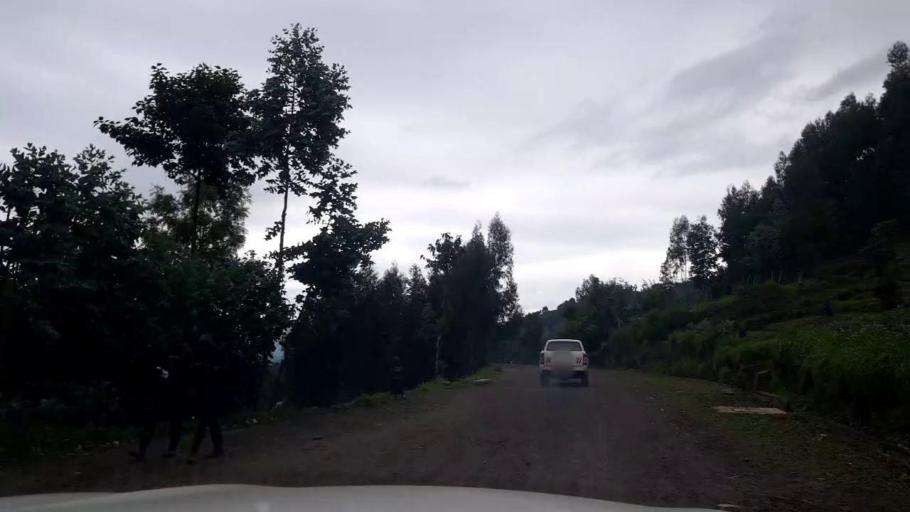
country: RW
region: Northern Province
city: Musanze
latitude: -1.5025
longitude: 29.5335
